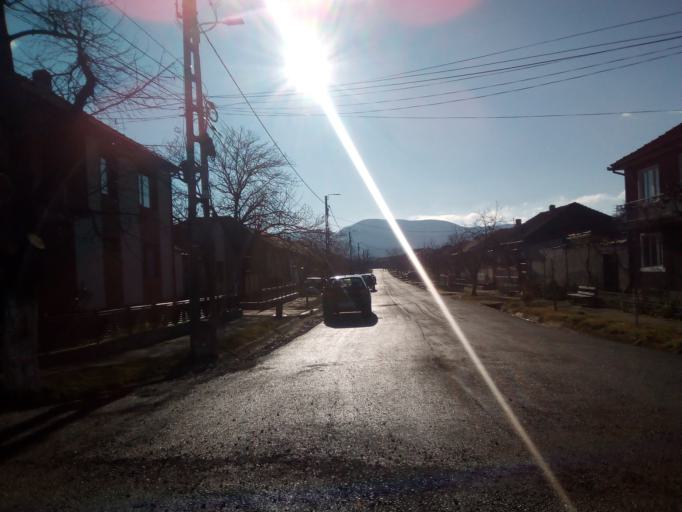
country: RO
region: Mehedinti
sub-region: Comuna Eselnita
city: Eselnita
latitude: 44.6993
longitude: 22.3631
